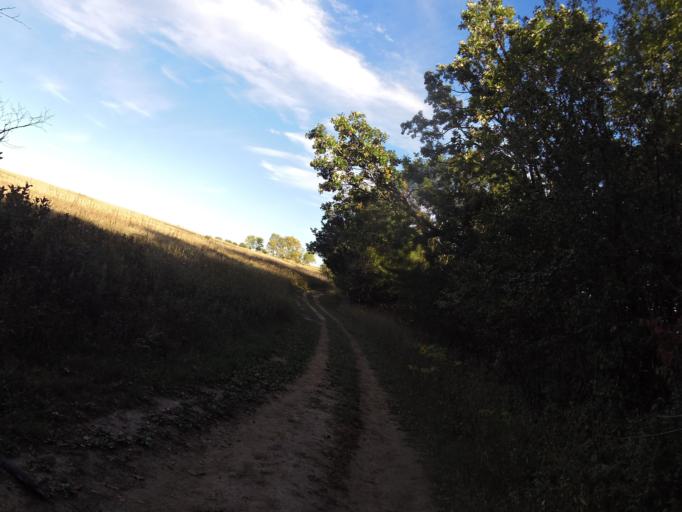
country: US
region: Minnesota
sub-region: Washington County
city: Afton
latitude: 44.8644
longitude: -92.7940
